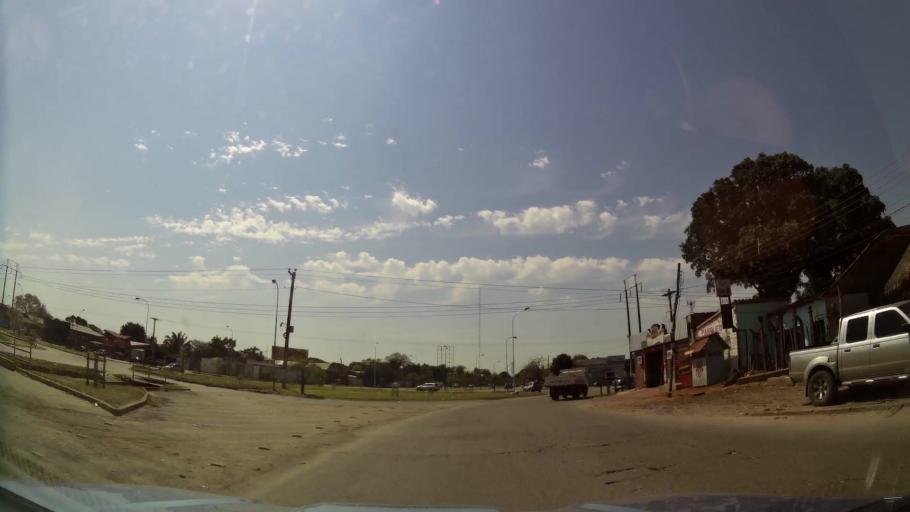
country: BO
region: Santa Cruz
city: Santa Cruz de la Sierra
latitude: -17.7442
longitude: -63.1610
